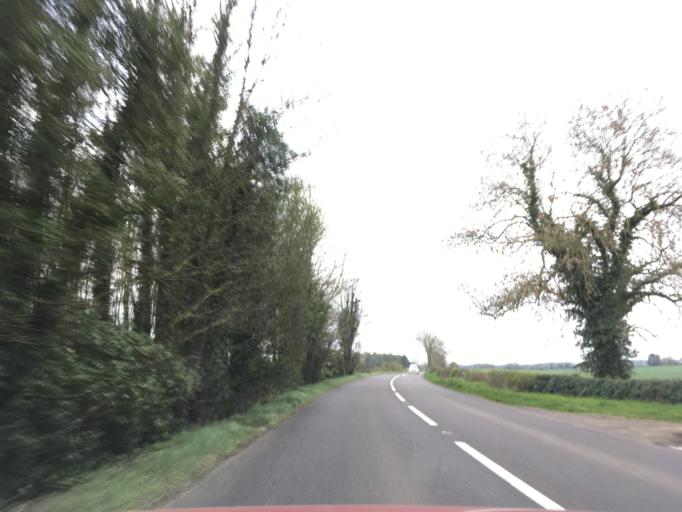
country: GB
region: England
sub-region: Gloucestershire
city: Coates
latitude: 51.6957
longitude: -2.0017
